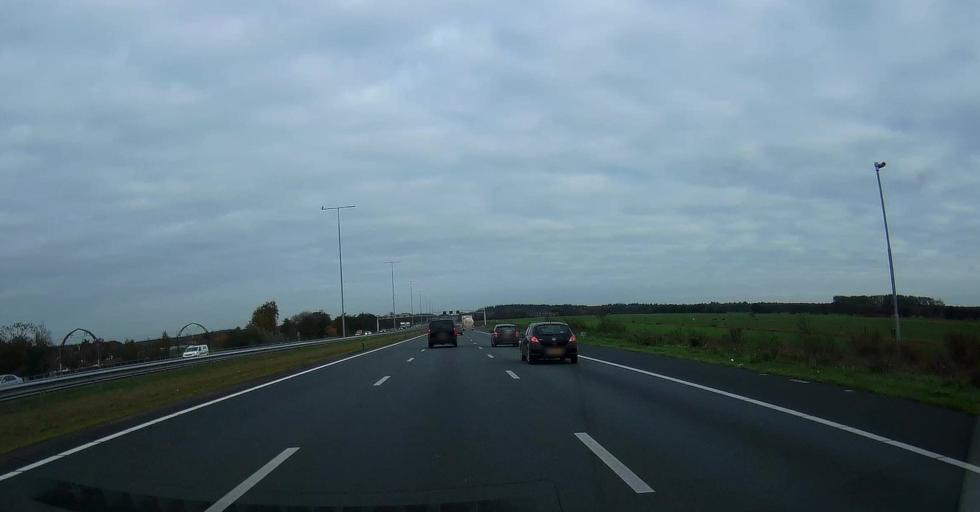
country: NL
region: North Holland
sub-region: Gemeente Wijdemeren
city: Nieuw-Loosdrecht
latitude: 52.1603
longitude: 5.1685
